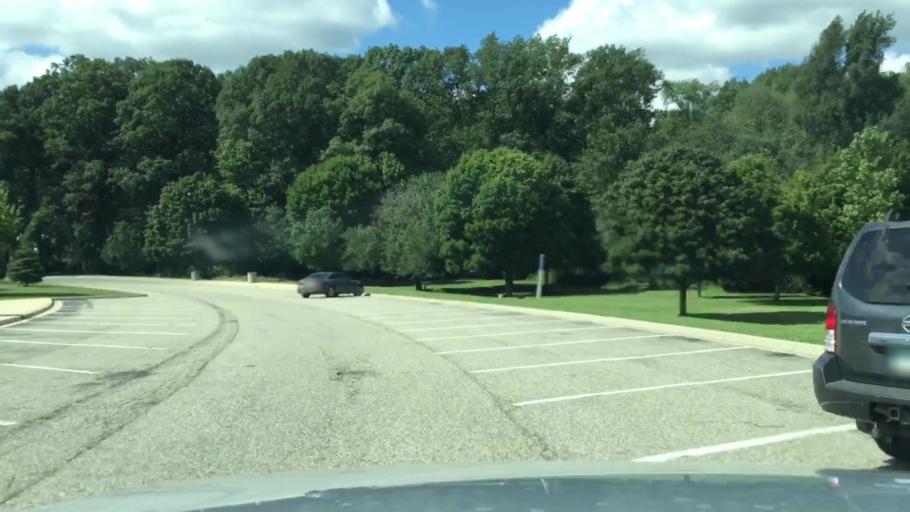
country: US
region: Michigan
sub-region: Calhoun County
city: Marshall
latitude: 42.2839
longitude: -84.9137
